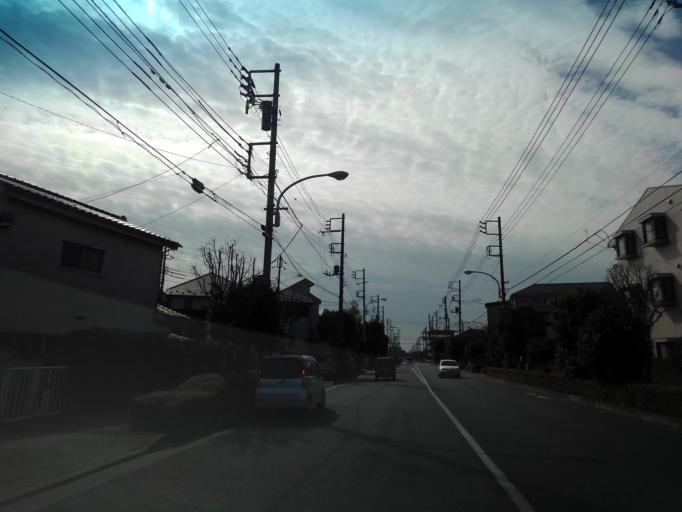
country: JP
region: Tokyo
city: Tanashicho
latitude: 35.7585
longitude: 139.5077
